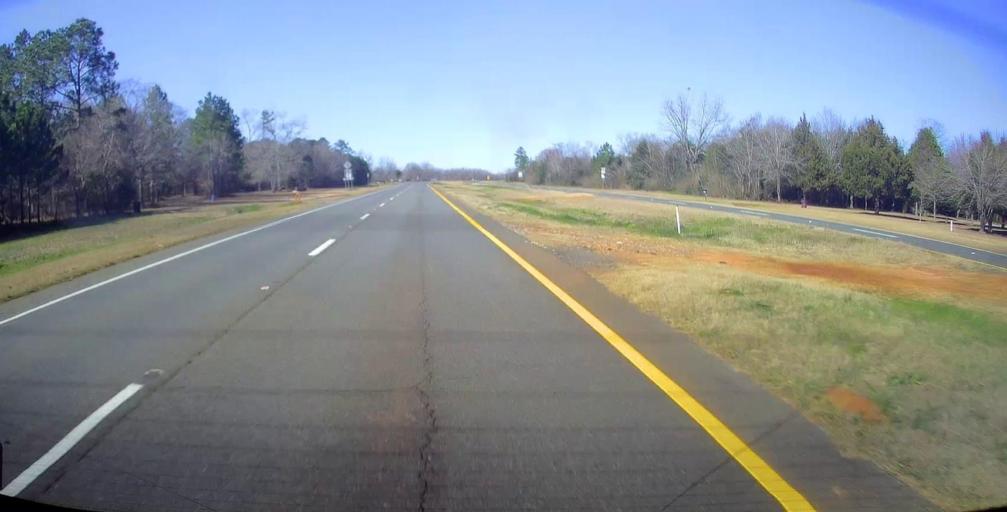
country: US
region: Georgia
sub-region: Sumter County
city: Americus
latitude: 32.1516
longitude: -84.2700
